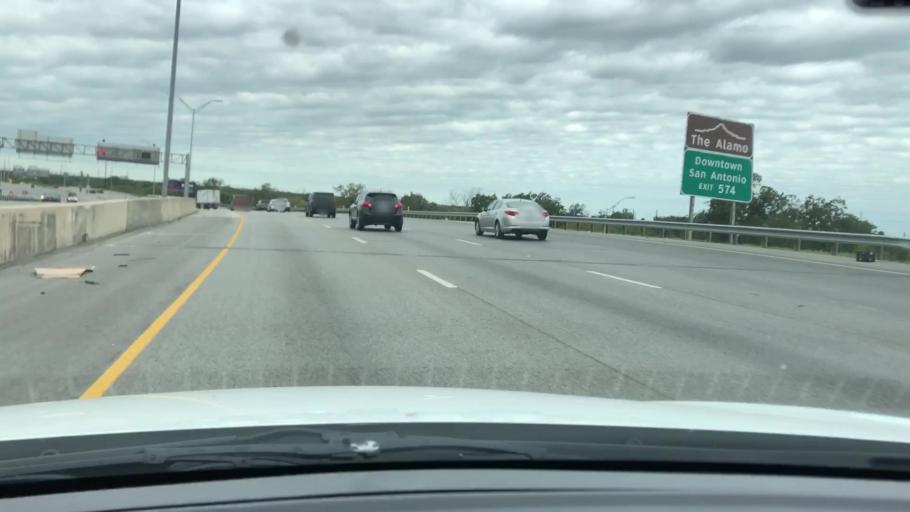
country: US
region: Texas
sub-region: Bexar County
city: San Antonio
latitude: 29.4014
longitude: -98.4704
